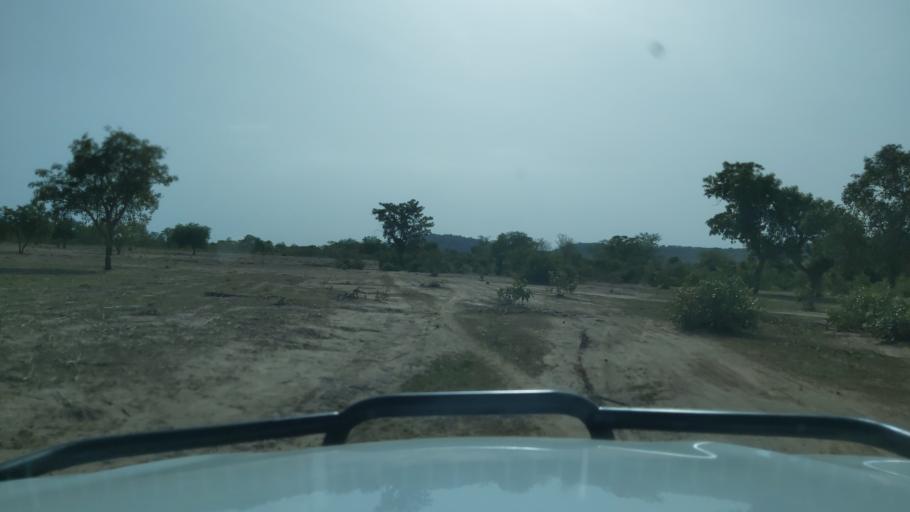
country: ML
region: Koulikoro
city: Koulikoro
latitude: 13.1756
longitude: -7.7479
